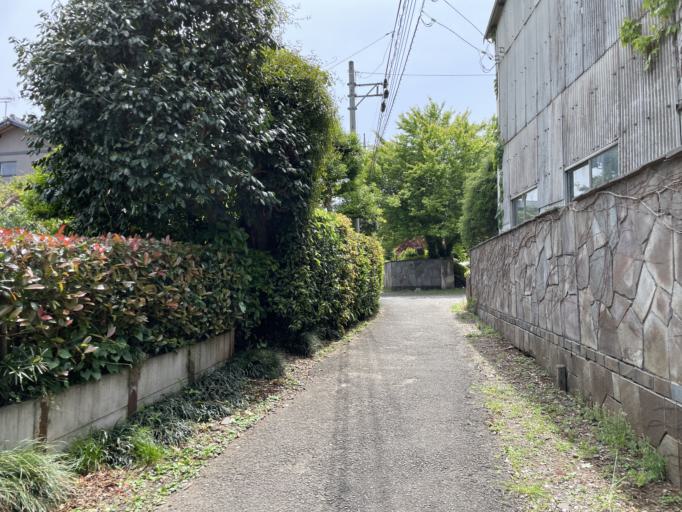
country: JP
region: Saitama
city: Morohongo
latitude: 35.8973
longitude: 139.3232
